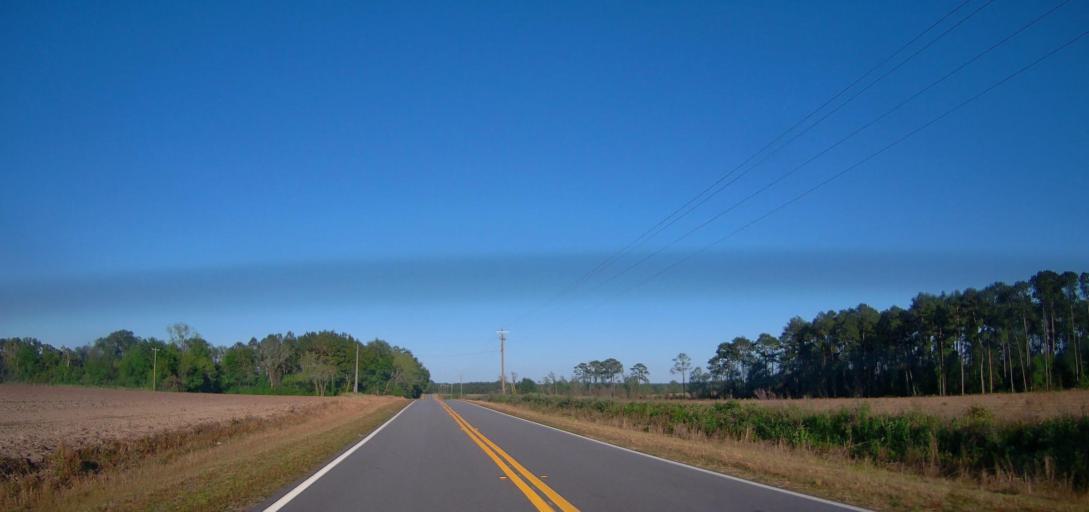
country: US
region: Georgia
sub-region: Ben Hill County
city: Fitzgerald
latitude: 31.6563
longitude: -83.1716
